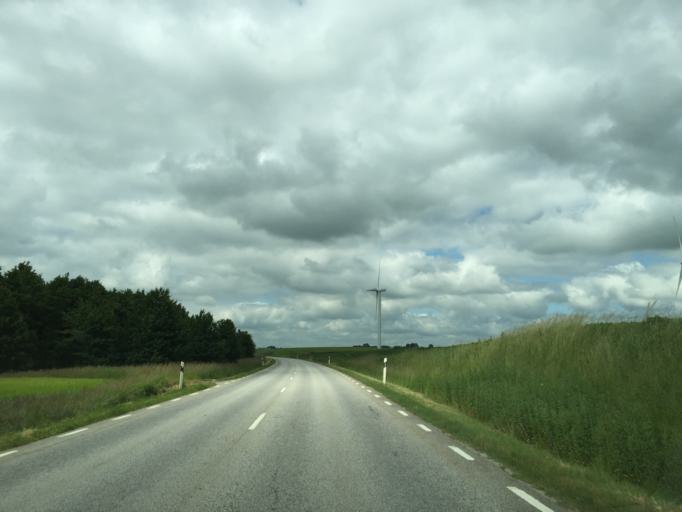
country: SE
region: Skane
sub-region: Svedala Kommun
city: Klagerup
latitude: 55.6066
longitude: 13.2660
